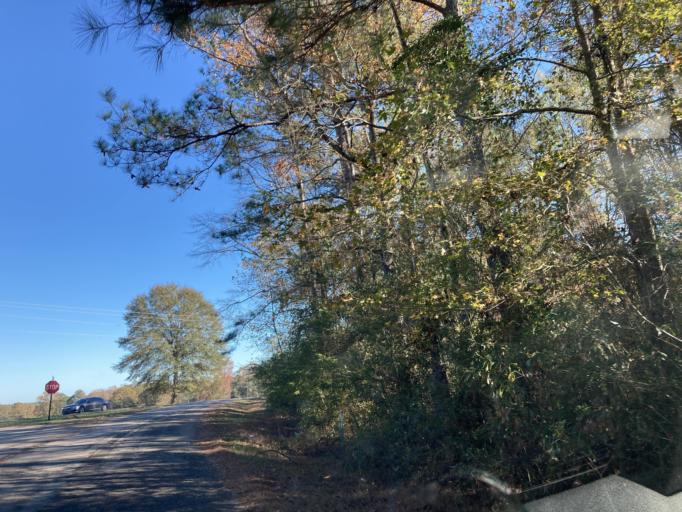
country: US
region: Mississippi
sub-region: Lamar County
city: Sumrall
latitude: 31.3110
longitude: -89.6585
